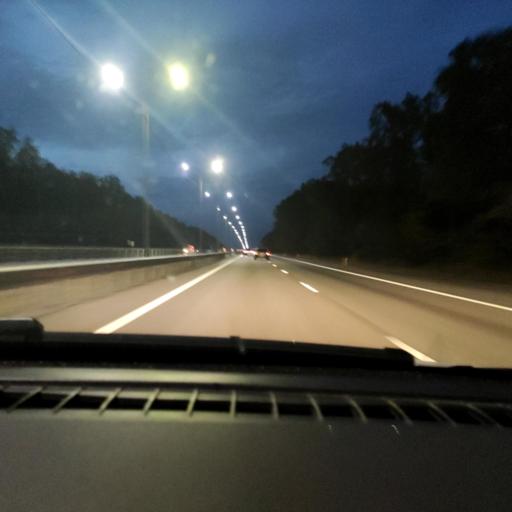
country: RU
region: Voronezj
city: Ramon'
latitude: 51.8748
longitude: 39.2168
